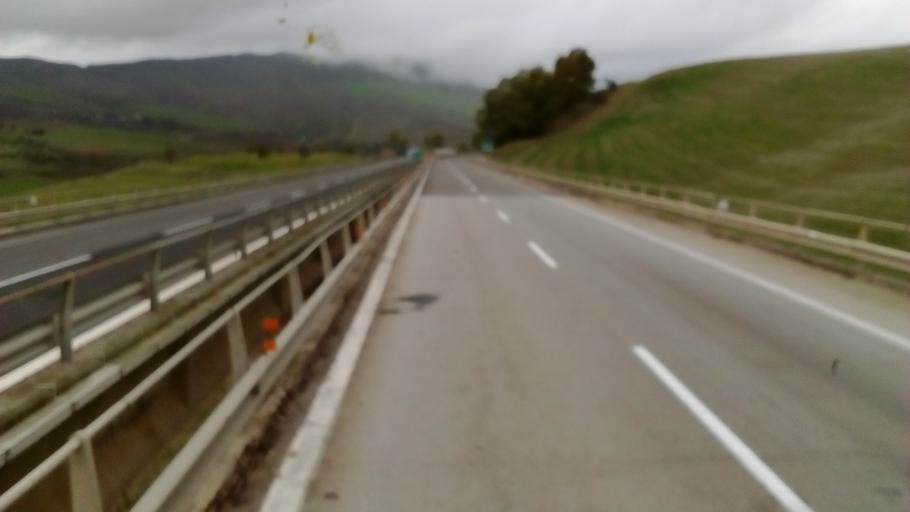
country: IT
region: Sicily
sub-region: Enna
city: Calascibetta
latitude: 37.5719
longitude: 14.2328
